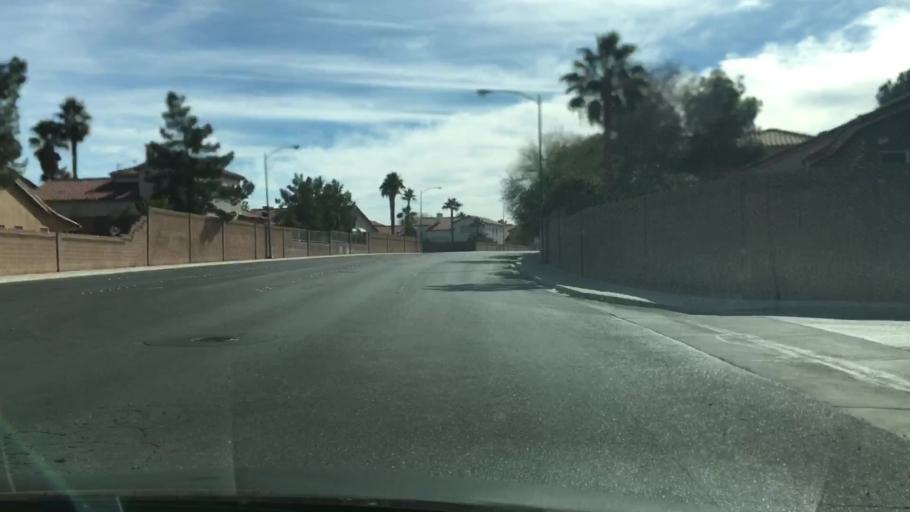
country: US
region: Nevada
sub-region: Clark County
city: Whitney
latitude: 36.0382
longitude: -115.1276
